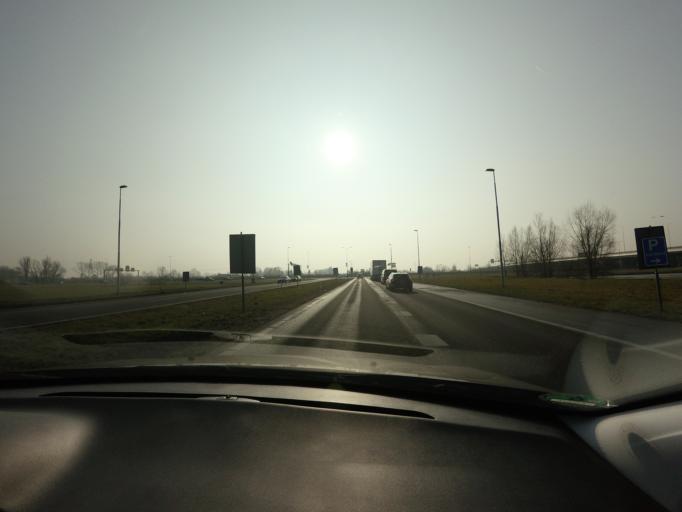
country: NL
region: Utrecht
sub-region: Stichtse Vecht
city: Vreeland
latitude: 52.2253
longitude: 4.9873
